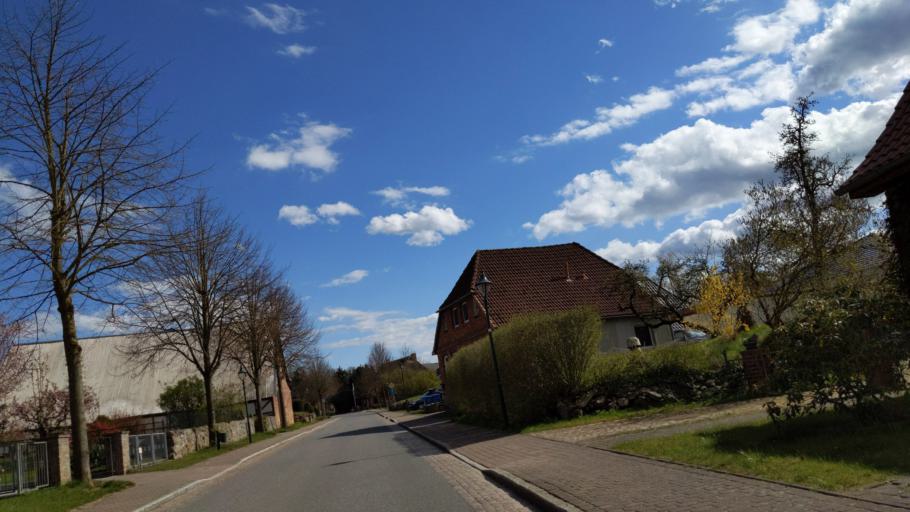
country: DE
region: Mecklenburg-Vorpommern
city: Selmsdorf
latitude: 53.8792
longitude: 10.8638
